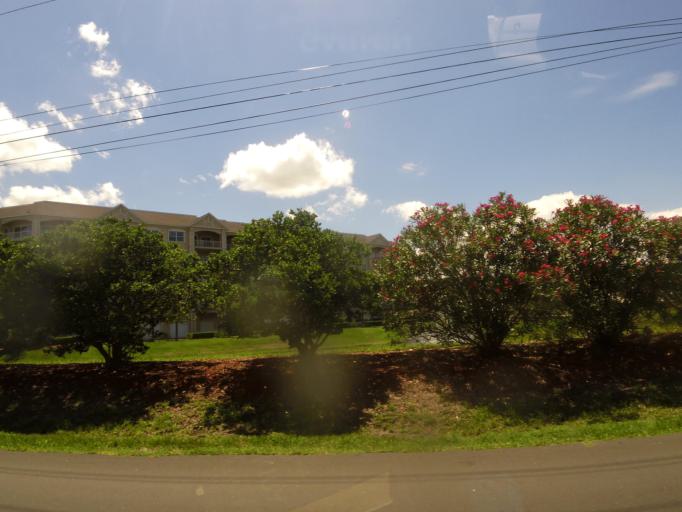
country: US
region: Florida
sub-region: Nassau County
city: Fernandina Beach
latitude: 30.6726
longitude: -81.4318
